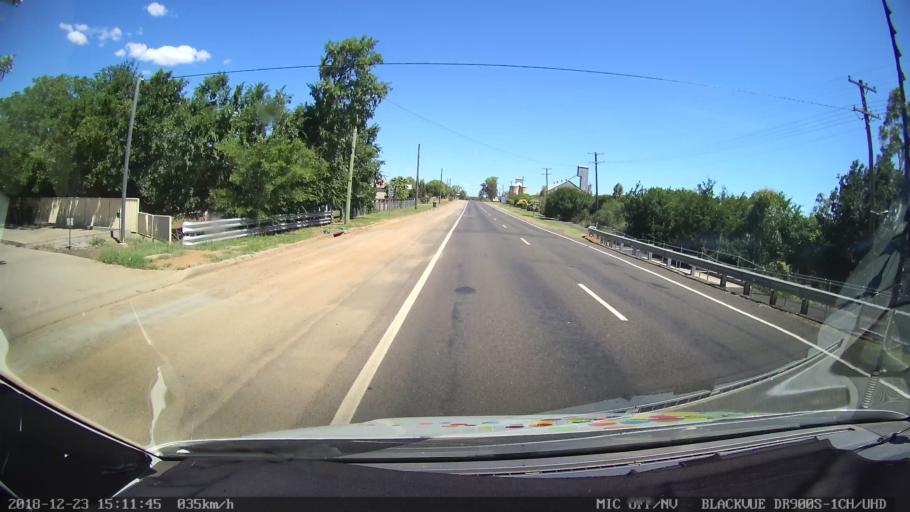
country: AU
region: New South Wales
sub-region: Tamworth Municipality
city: Manilla
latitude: -30.7506
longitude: 150.7260
